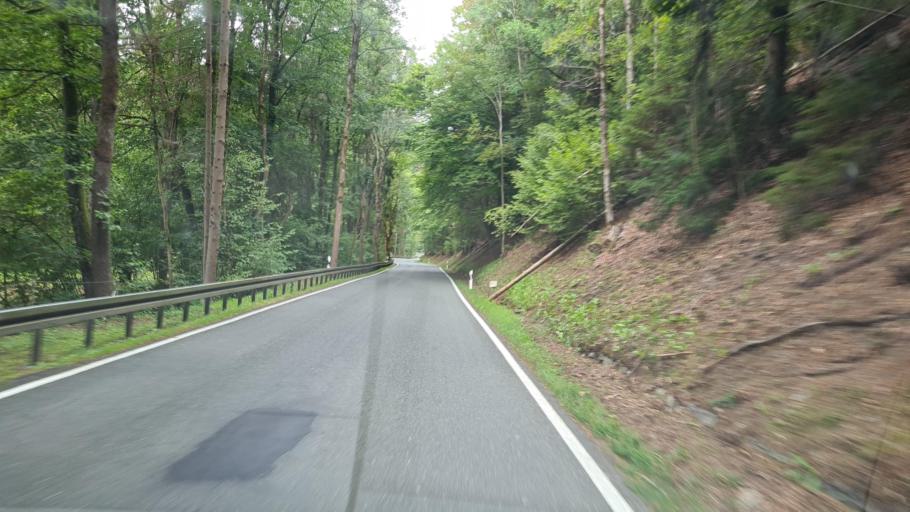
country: DE
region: Thuringia
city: Leutenberg
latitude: 50.5497
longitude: 11.4744
